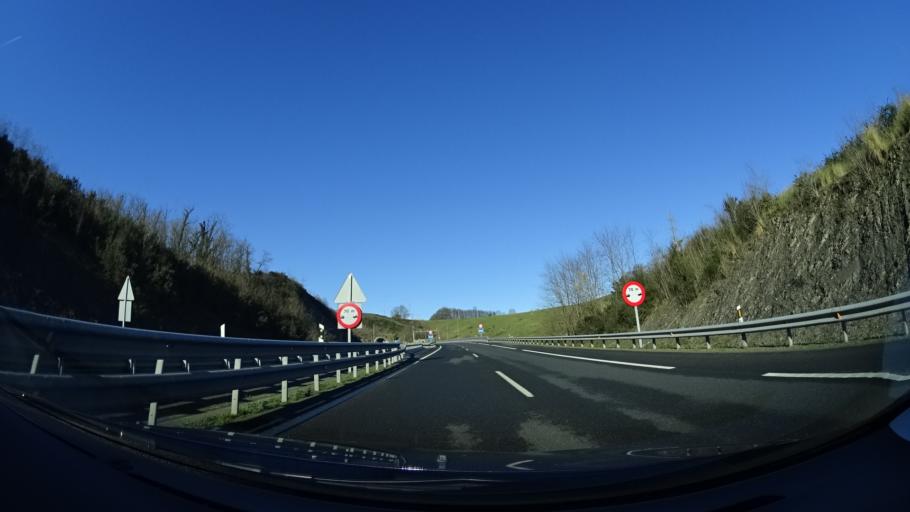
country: ES
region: Basque Country
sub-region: Provincia de Guipuzcoa
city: Lasarte
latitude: 43.2811
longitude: -2.0236
